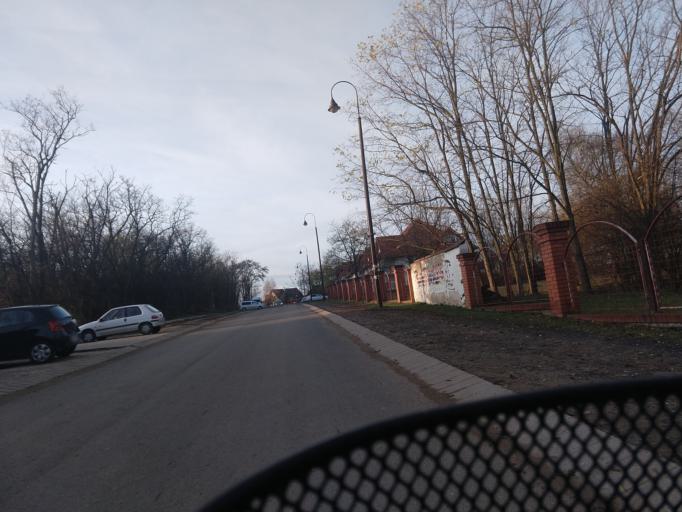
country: HU
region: Pest
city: Orbottyan
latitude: 47.6626
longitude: 19.2718
